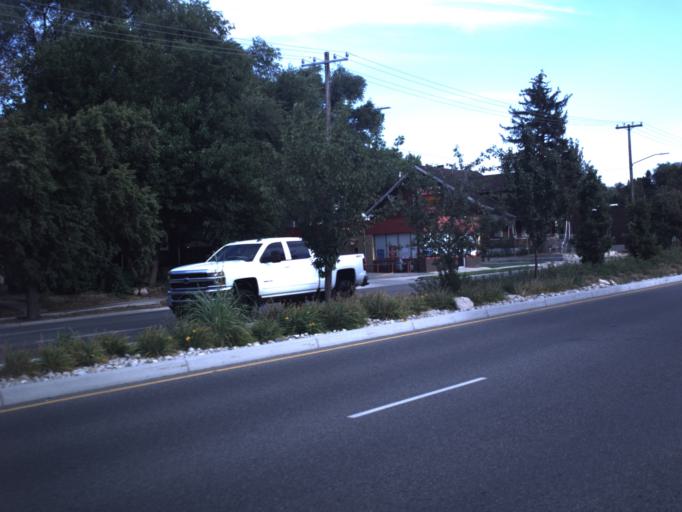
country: US
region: Utah
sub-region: Salt Lake County
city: Salt Lake City
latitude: 40.7797
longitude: -111.8998
